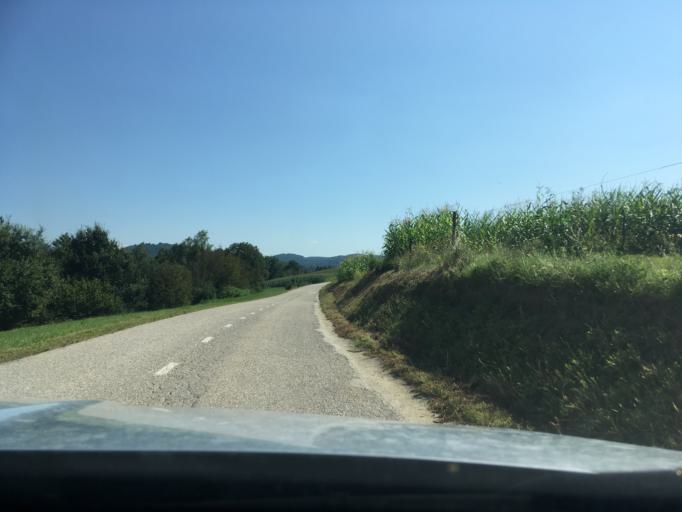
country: SI
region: Metlika
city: Metlika
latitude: 45.5650
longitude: 15.2968
